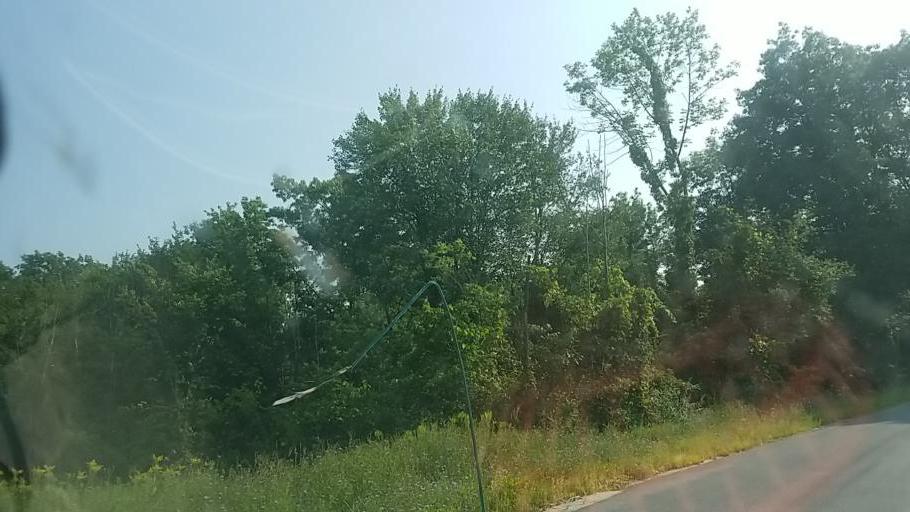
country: US
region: New York
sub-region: Montgomery County
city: Tribes Hill
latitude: 42.9226
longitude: -74.3271
